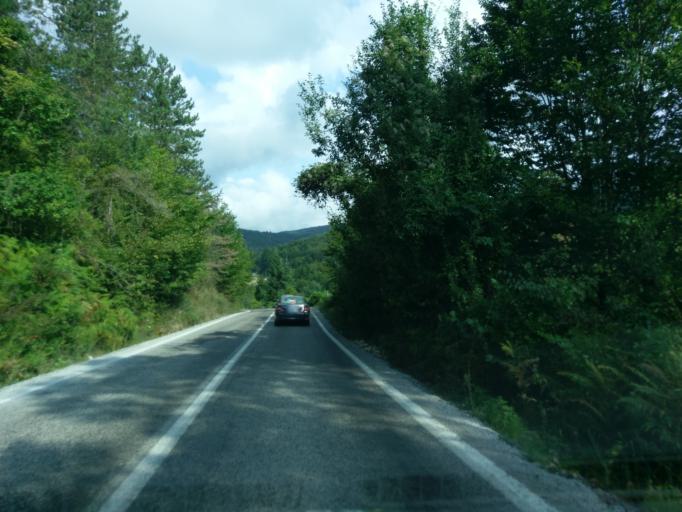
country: TR
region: Sinop
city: Ayancik
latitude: 41.8827
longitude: 34.5199
